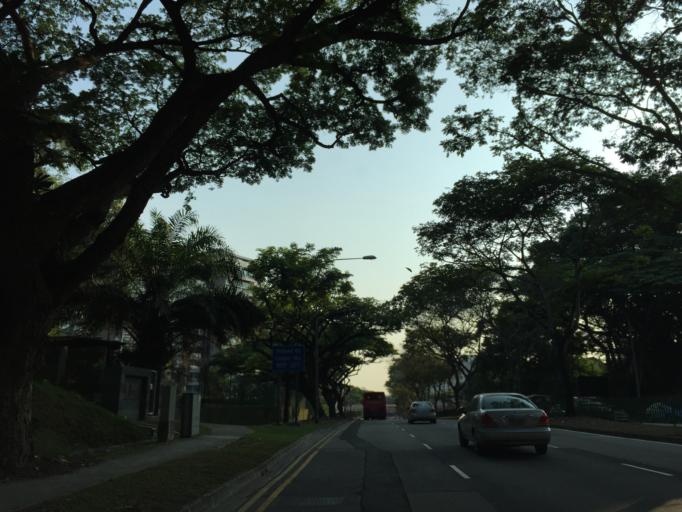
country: SG
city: Singapore
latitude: 1.3070
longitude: 103.8021
